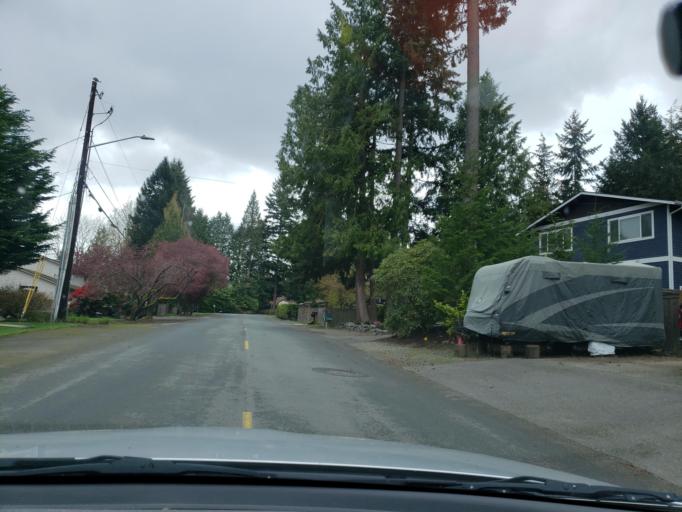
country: US
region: Washington
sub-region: Snohomish County
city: Meadowdale
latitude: 47.8335
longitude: -122.3443
